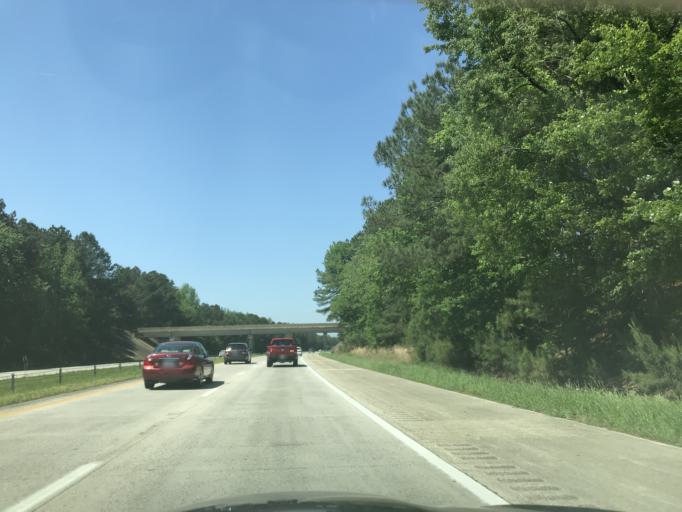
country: US
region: North Carolina
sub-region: Johnston County
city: Benson
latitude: 35.4709
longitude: -78.5488
